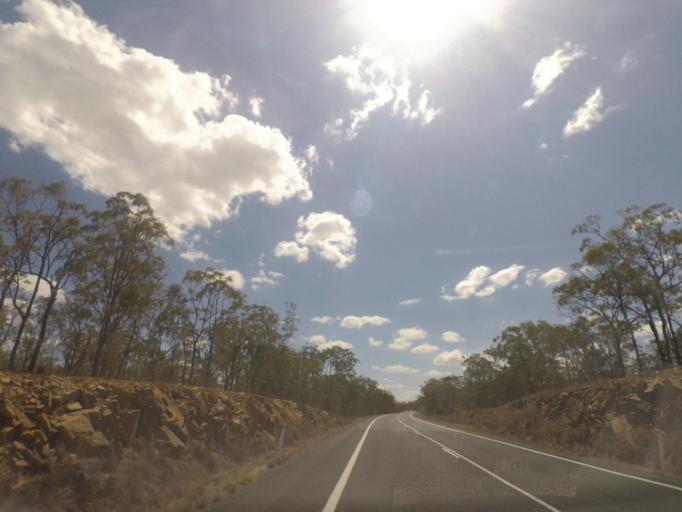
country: AU
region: Queensland
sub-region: Southern Downs
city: Warwick
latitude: -28.1628
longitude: 151.6809
